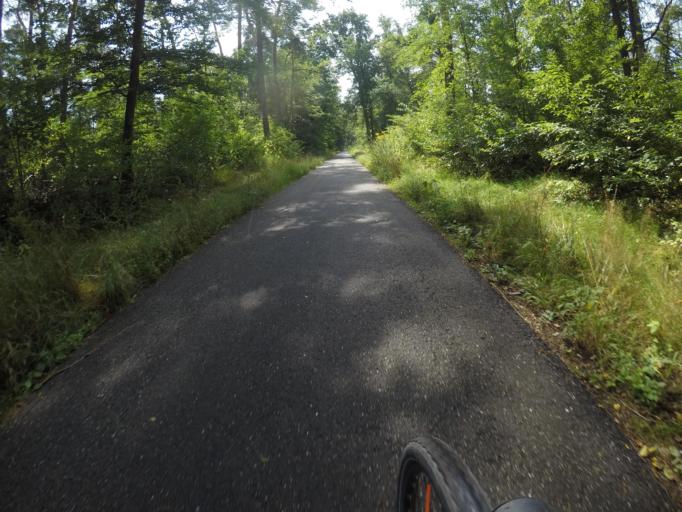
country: DE
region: Baden-Wuerttemberg
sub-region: Karlsruhe Region
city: Reilingen
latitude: 49.3203
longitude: 8.5982
